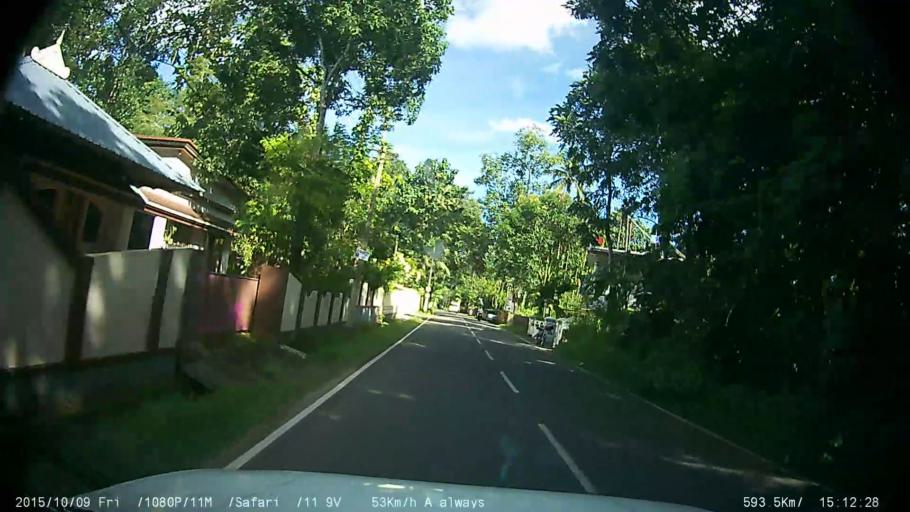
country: IN
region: Kerala
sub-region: Ernakulam
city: Piravam
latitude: 9.8714
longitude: 76.5852
